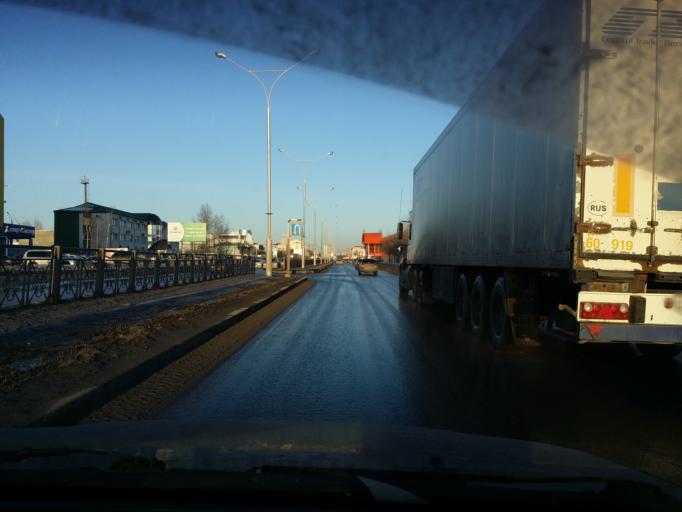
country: RU
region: Khanty-Mansiyskiy Avtonomnyy Okrug
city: Nizhnevartovsk
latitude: 60.9390
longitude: 76.5353
